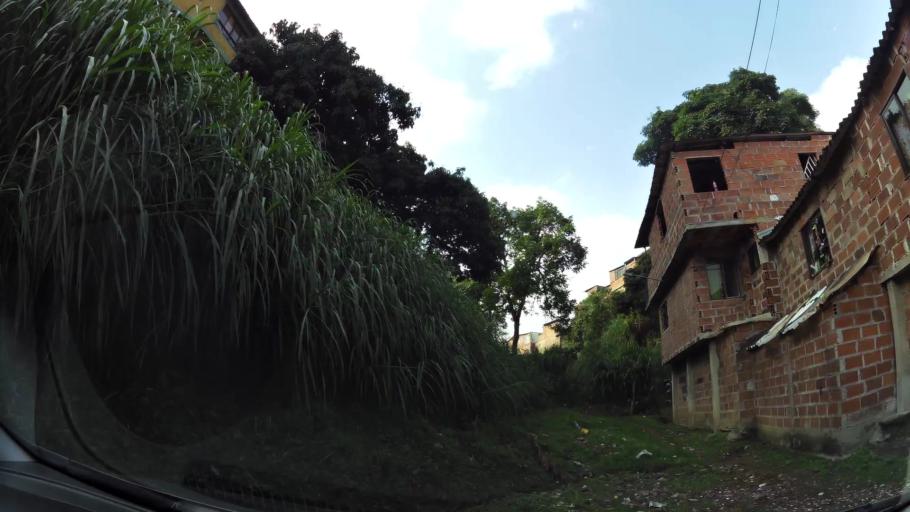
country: CO
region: Antioquia
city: Sabaneta
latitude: 6.1624
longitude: -75.6259
